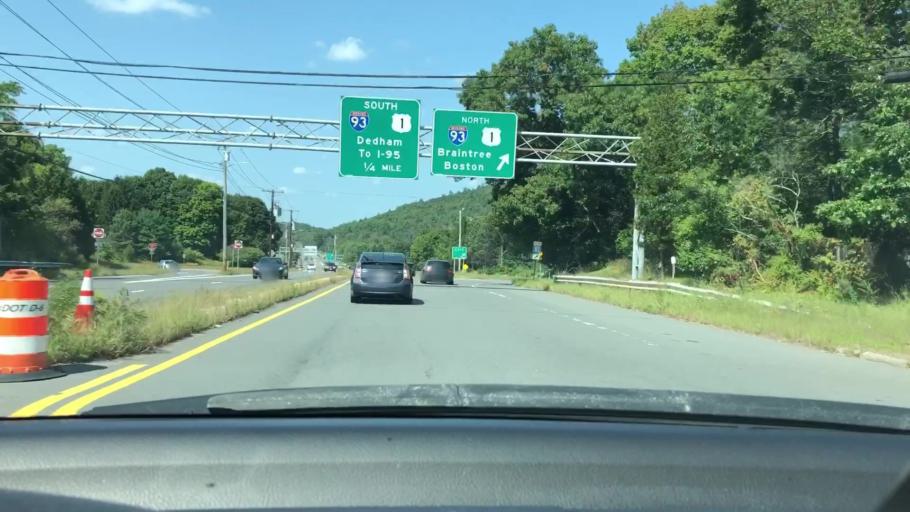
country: US
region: Massachusetts
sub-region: Norfolk County
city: Canton
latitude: 42.1998
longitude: -71.1190
